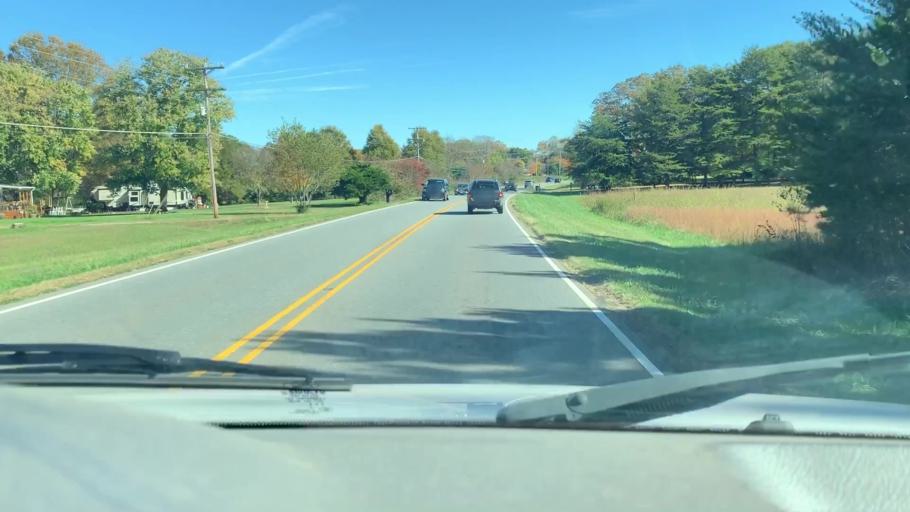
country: US
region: North Carolina
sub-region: Lincoln County
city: Lowesville
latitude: 35.4283
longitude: -80.9280
